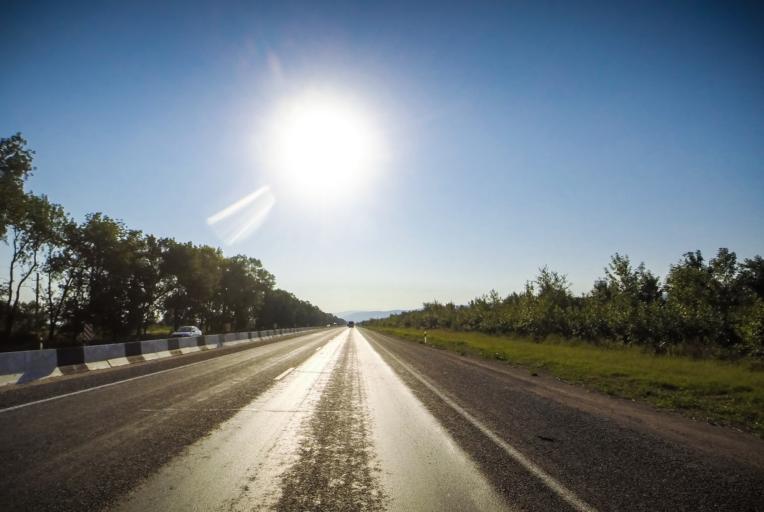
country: RU
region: Kabardino-Balkariya
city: Urukh
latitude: 43.3221
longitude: 44.0883
